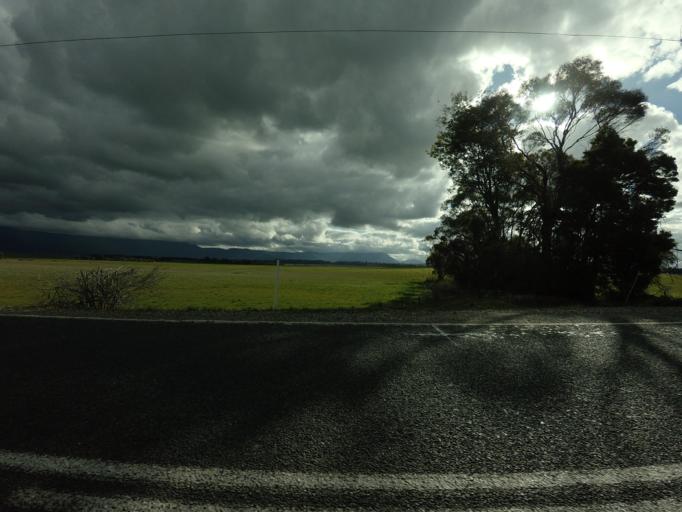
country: AU
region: Tasmania
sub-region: Northern Midlands
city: Longford
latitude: -41.7418
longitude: 147.0823
